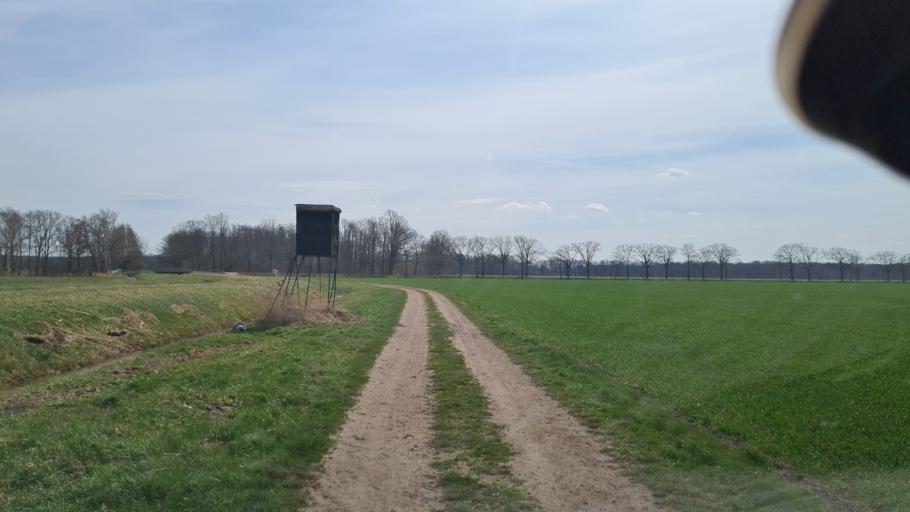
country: DE
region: Brandenburg
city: Bronkow
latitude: 51.6213
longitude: 13.9170
